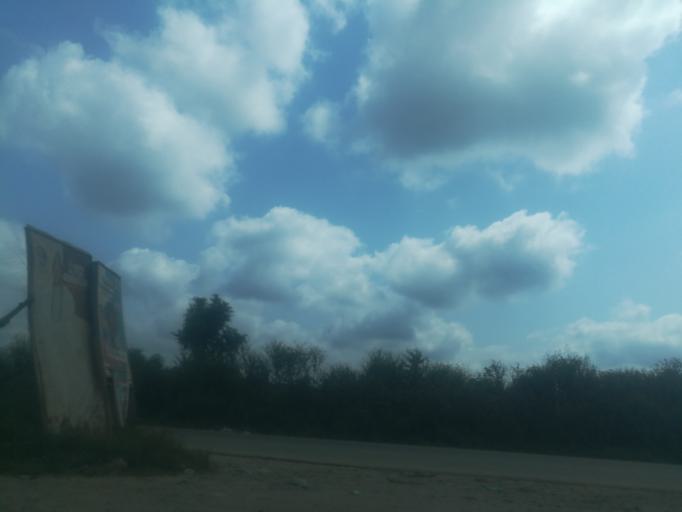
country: NG
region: Oyo
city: Moniya
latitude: 7.5854
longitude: 3.9152
